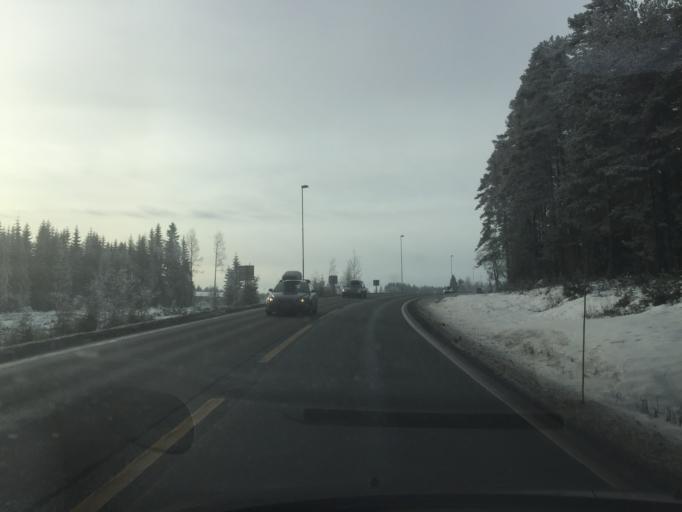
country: NO
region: Hedmark
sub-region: Loten
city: Loten
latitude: 60.8671
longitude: 11.4263
